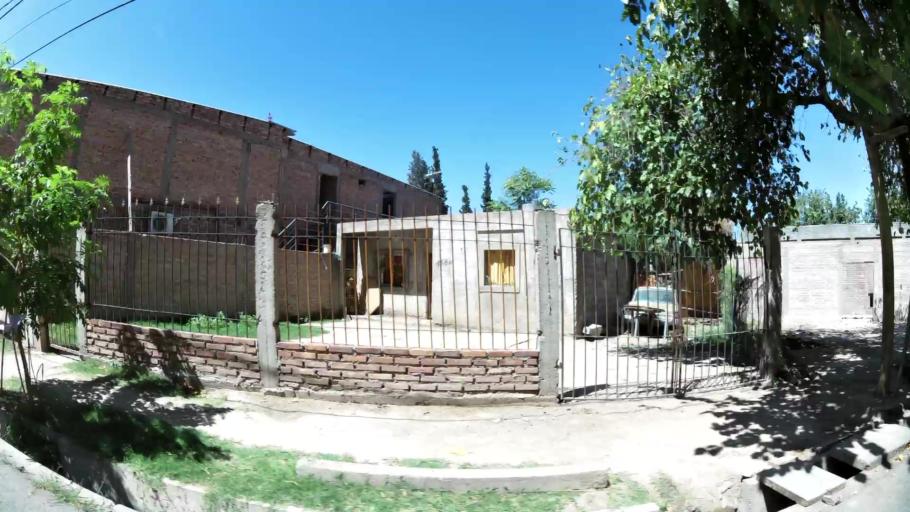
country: AR
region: San Juan
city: San Juan
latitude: -31.5253
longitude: -68.5546
